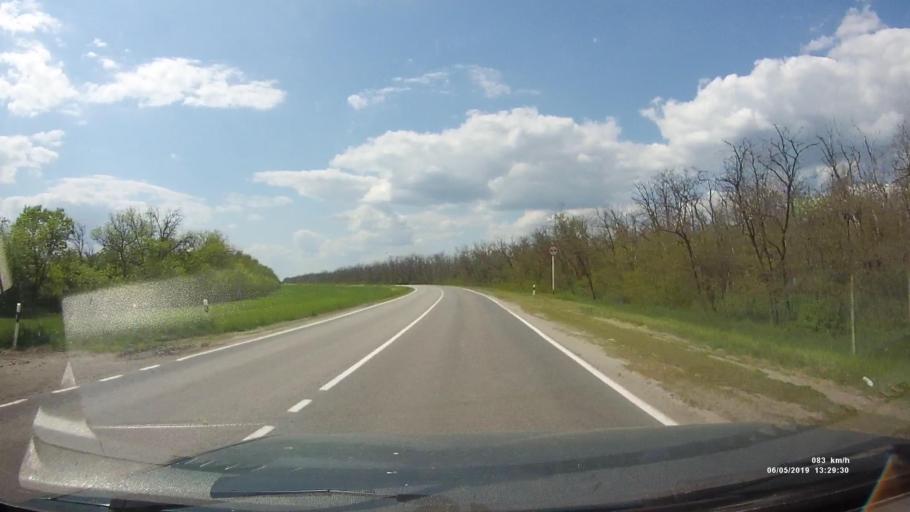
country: RU
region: Rostov
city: Ust'-Donetskiy
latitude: 47.6714
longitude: 40.8435
